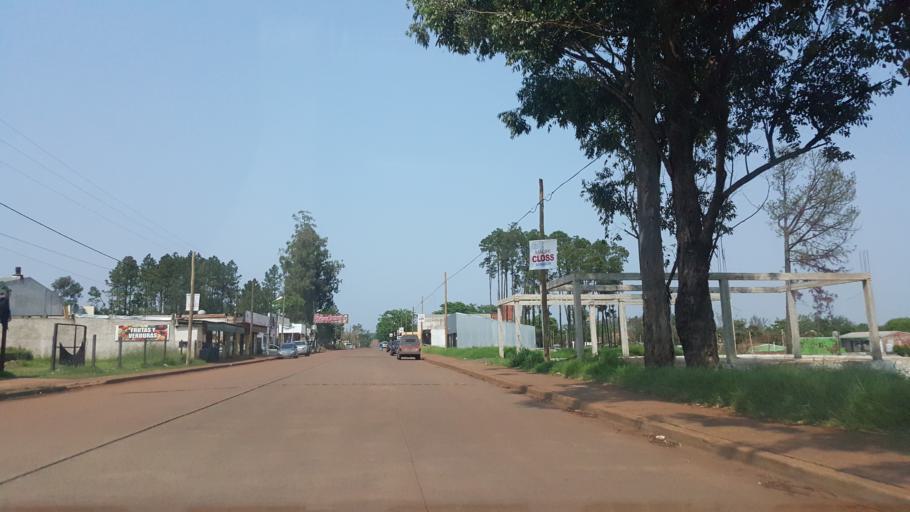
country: AR
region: Misiones
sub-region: Departamento de Capital
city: Posadas
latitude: -27.4157
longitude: -55.9565
